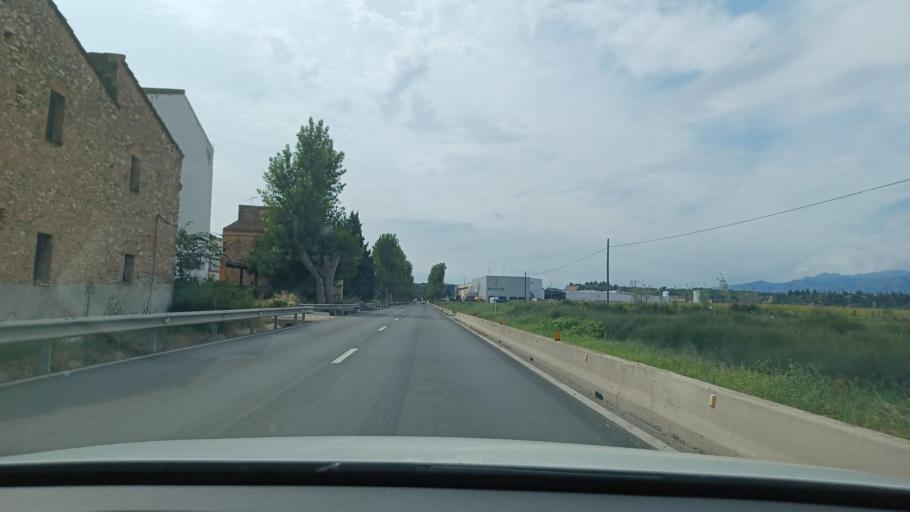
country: ES
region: Catalonia
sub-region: Provincia de Tarragona
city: Tortosa
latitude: 40.8005
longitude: 0.5013
